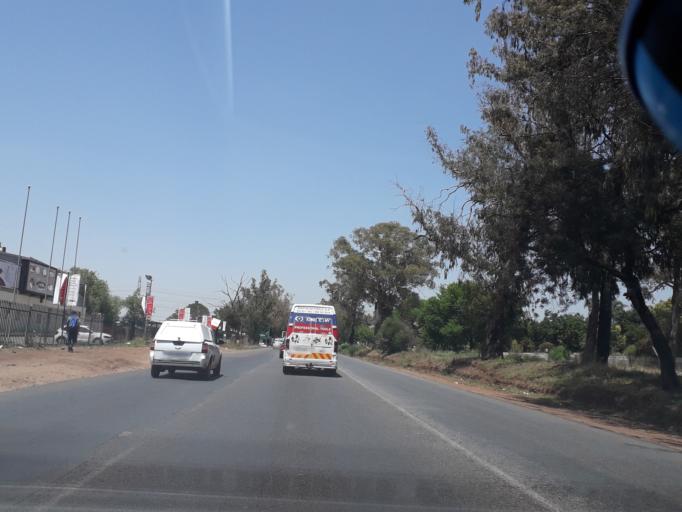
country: ZA
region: Gauteng
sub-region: City of Tshwane Metropolitan Municipality
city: Centurion
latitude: -25.8869
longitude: 28.1609
